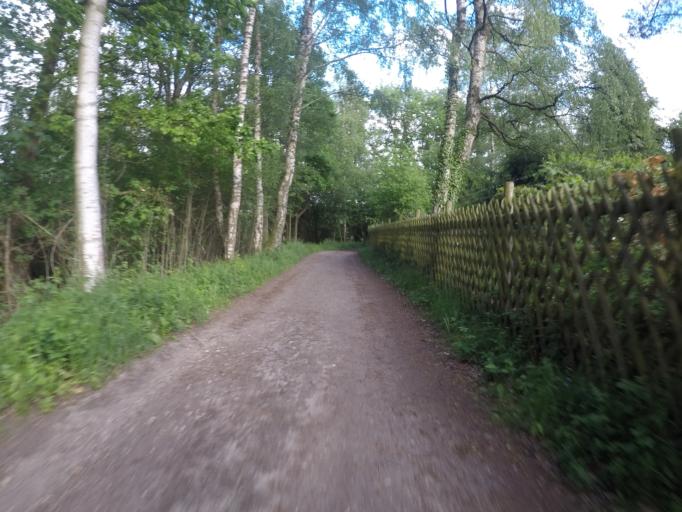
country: DE
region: Schleswig-Holstein
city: Bonningstedt
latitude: 53.6778
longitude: 9.9307
